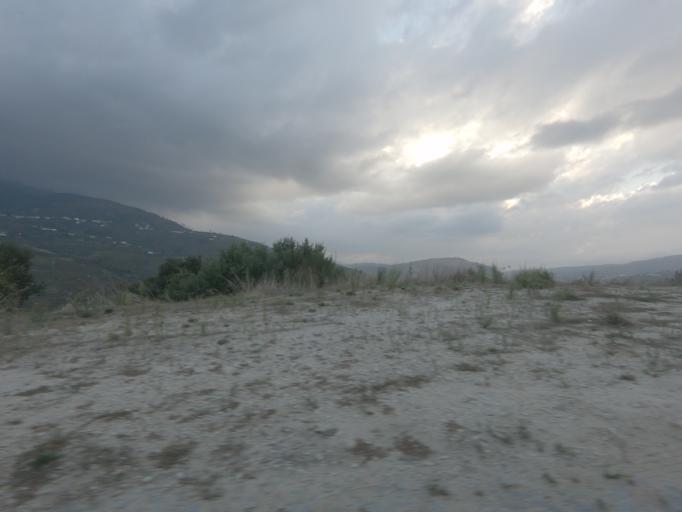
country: PT
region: Vila Real
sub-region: Mesao Frio
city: Mesao Frio
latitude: 41.1616
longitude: -7.8518
